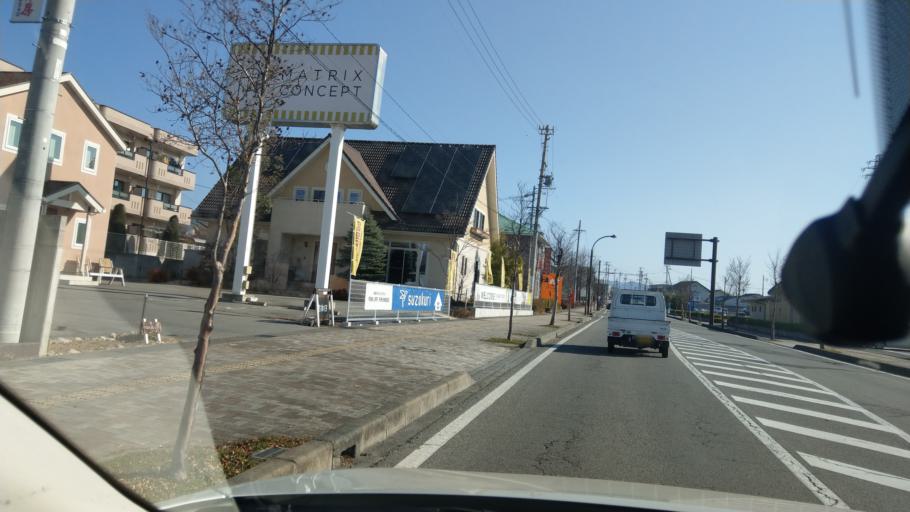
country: JP
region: Nagano
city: Komoro
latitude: 36.2769
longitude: 138.4676
